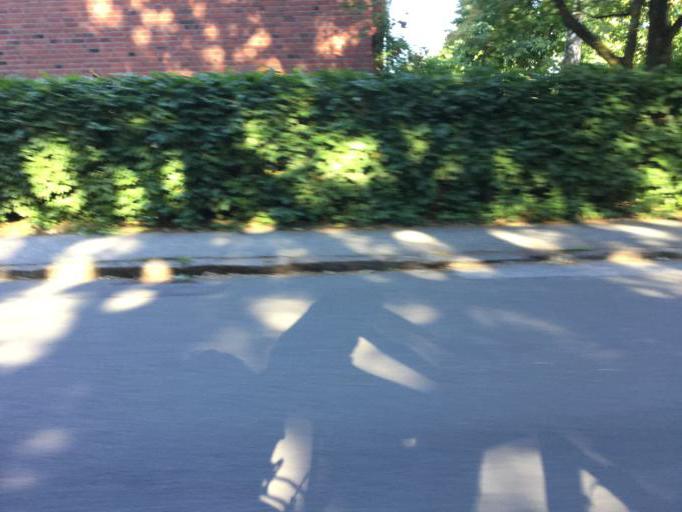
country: DE
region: Hamburg
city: Langenhorn
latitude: 53.6655
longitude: 10.0202
